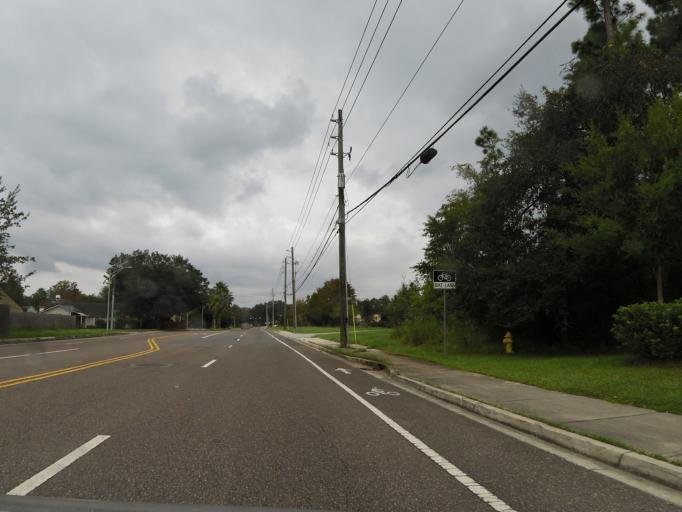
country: US
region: Florida
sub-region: Clay County
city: Bellair-Meadowbrook Terrace
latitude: 30.1996
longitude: -81.7648
